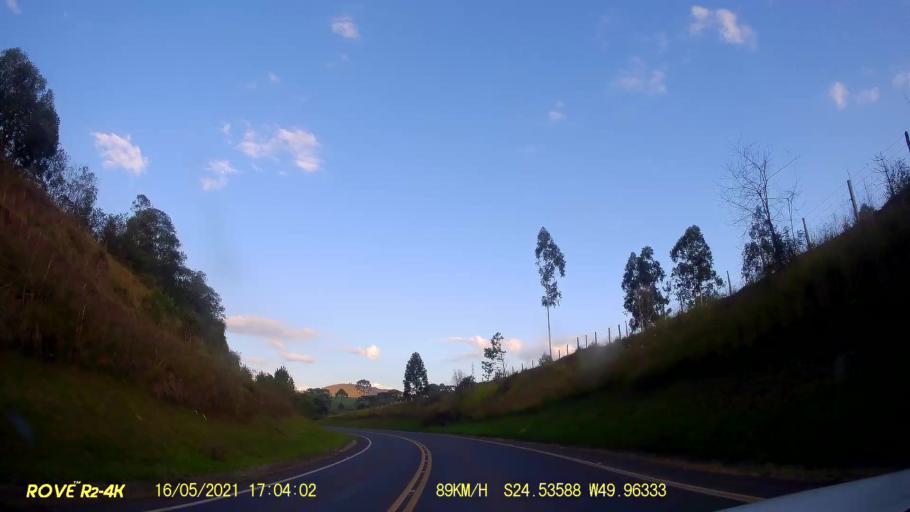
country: BR
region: Parana
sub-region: Pirai Do Sul
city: Pirai do Sul
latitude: -24.5363
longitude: -49.9636
